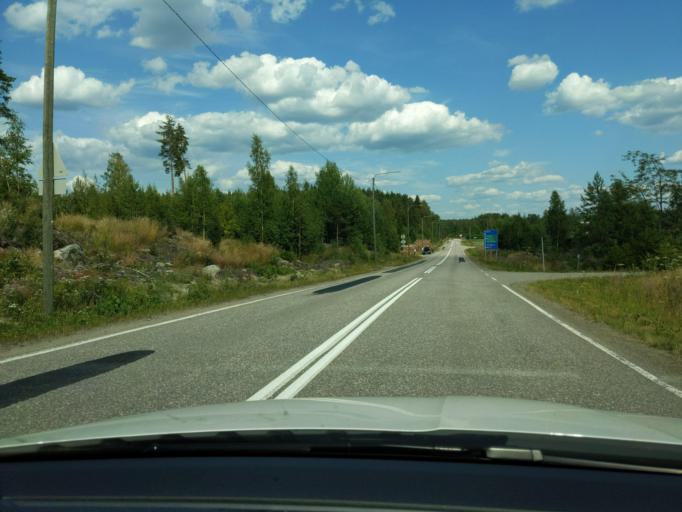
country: FI
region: Paijanne Tavastia
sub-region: Lahti
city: Heinola
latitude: 61.3313
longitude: 26.1602
